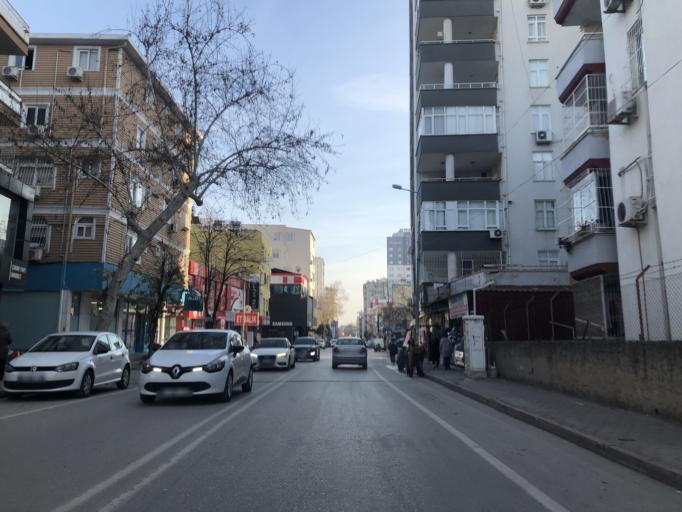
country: TR
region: Adana
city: Adana
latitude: 37.0249
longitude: 35.3125
